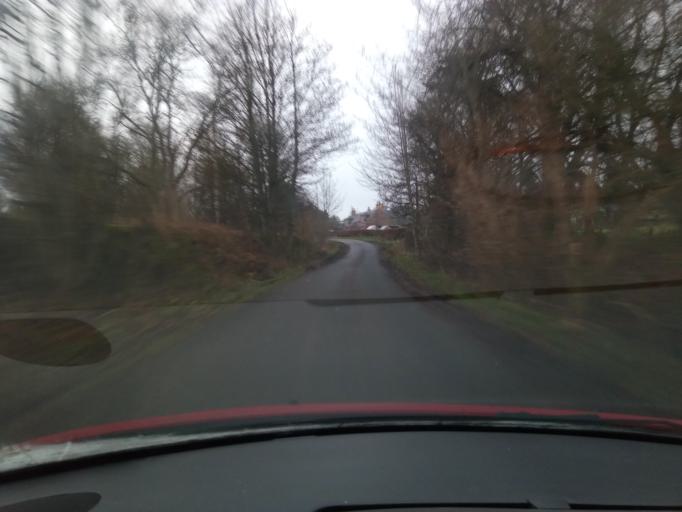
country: GB
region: Scotland
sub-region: The Scottish Borders
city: Kelso
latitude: 55.5509
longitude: -2.4320
